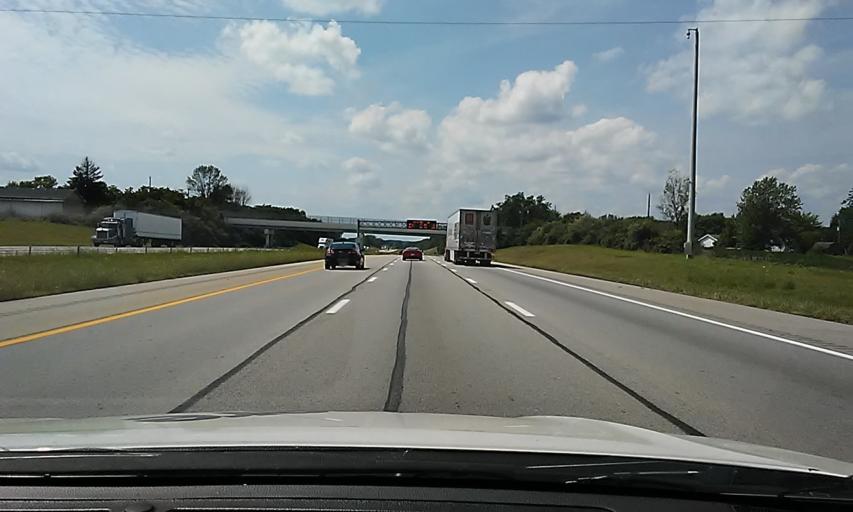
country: US
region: Ohio
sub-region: Clark County
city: Lisbon
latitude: 39.9350
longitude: -83.6438
